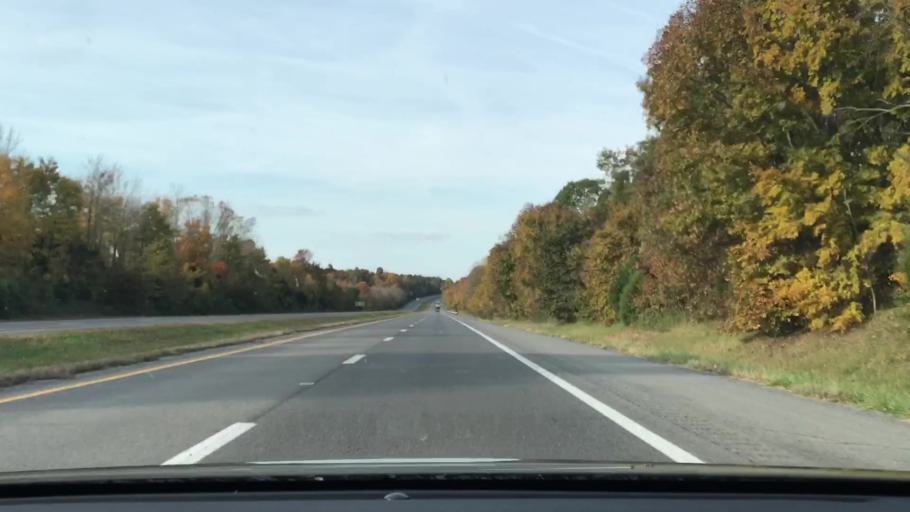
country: US
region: Kentucky
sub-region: Marshall County
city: Benton
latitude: 36.8448
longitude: -88.4093
